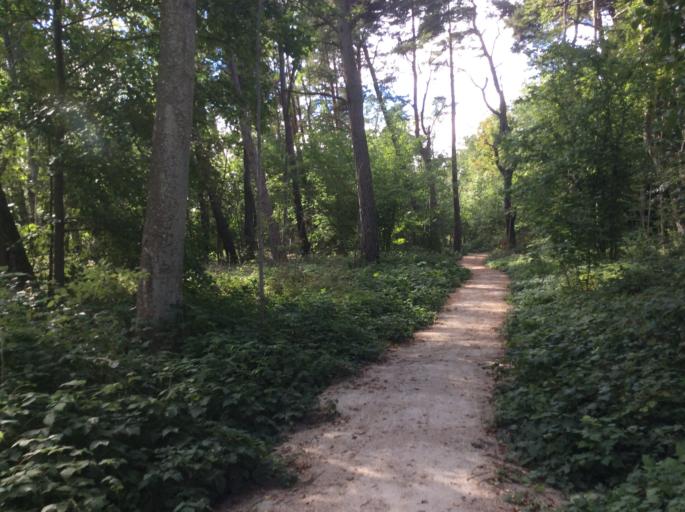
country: SE
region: Gotland
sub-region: Gotland
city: Vibble
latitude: 57.6190
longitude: 18.2693
